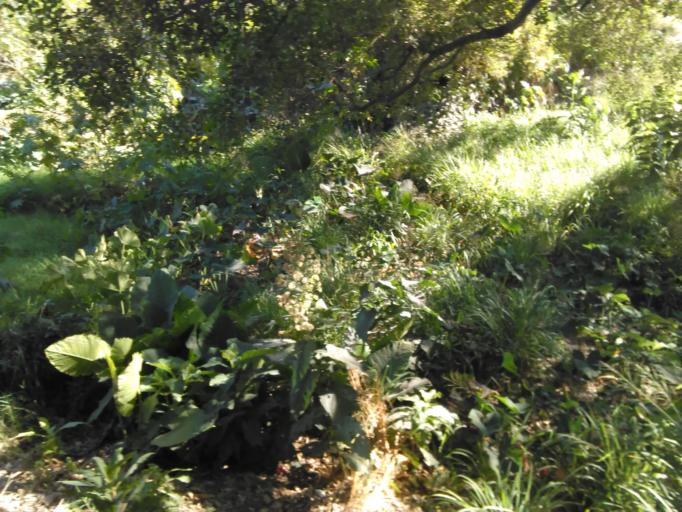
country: MX
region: Nayarit
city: Tepic
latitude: 21.5126
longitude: -104.9169
